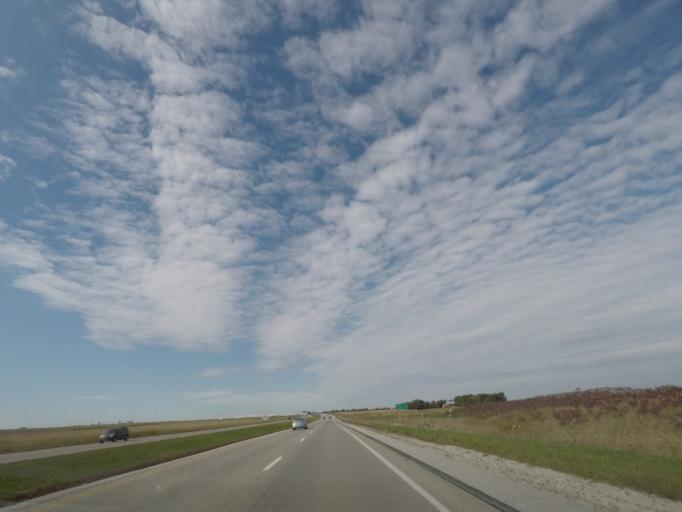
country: US
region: Iowa
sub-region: Story County
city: Gilbert
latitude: 42.0235
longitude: -93.7522
